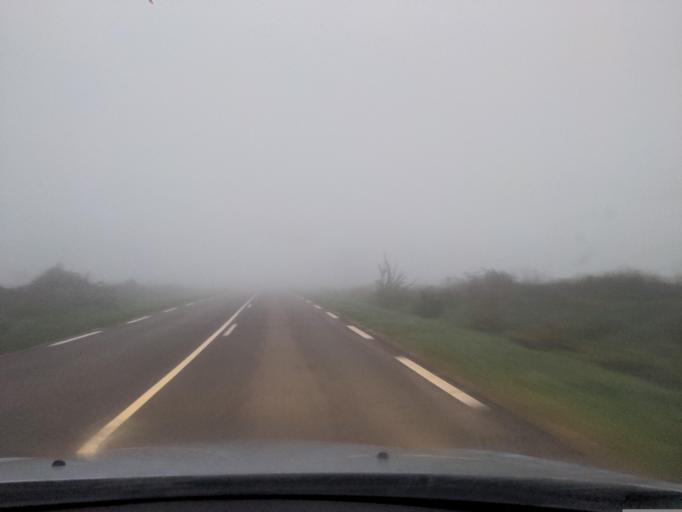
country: FR
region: Champagne-Ardenne
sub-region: Departement de la Haute-Marne
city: Langres
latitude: 47.8079
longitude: 5.2632
